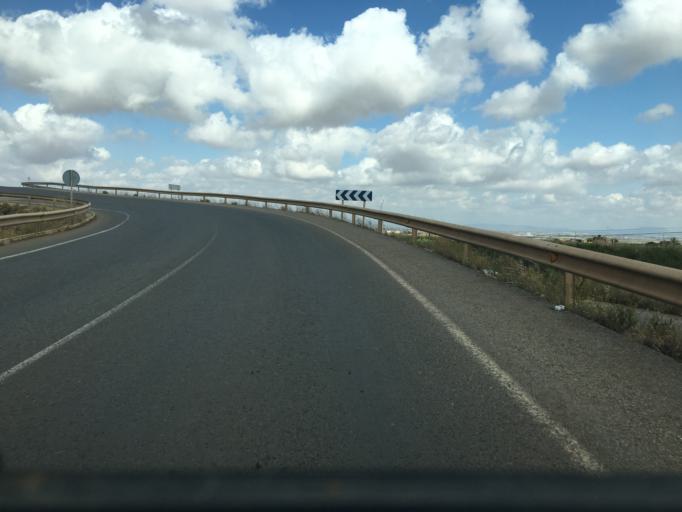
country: ES
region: Murcia
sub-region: Murcia
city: La Union
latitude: 37.6511
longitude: -0.8822
